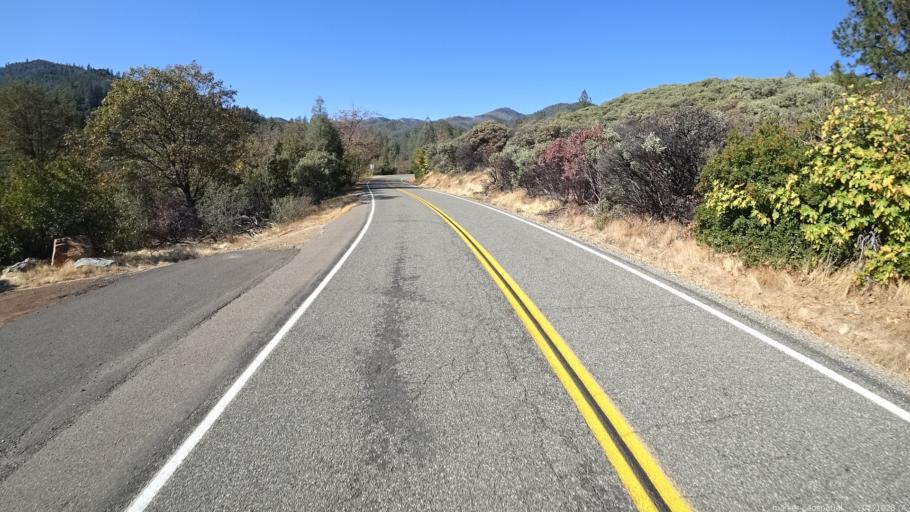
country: US
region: California
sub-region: Shasta County
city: Shasta
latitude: 40.6565
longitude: -122.4642
